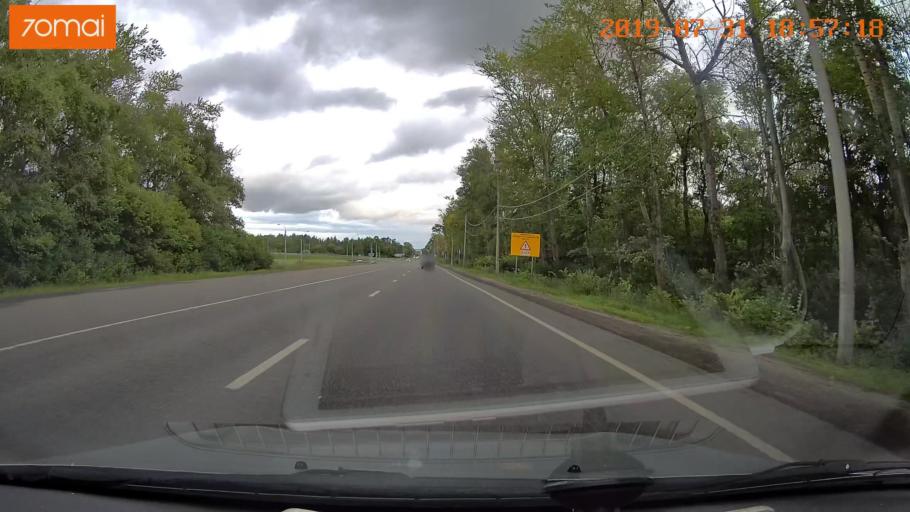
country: RU
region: Moskovskaya
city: Raduzhnyy
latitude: 55.1552
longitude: 38.6904
